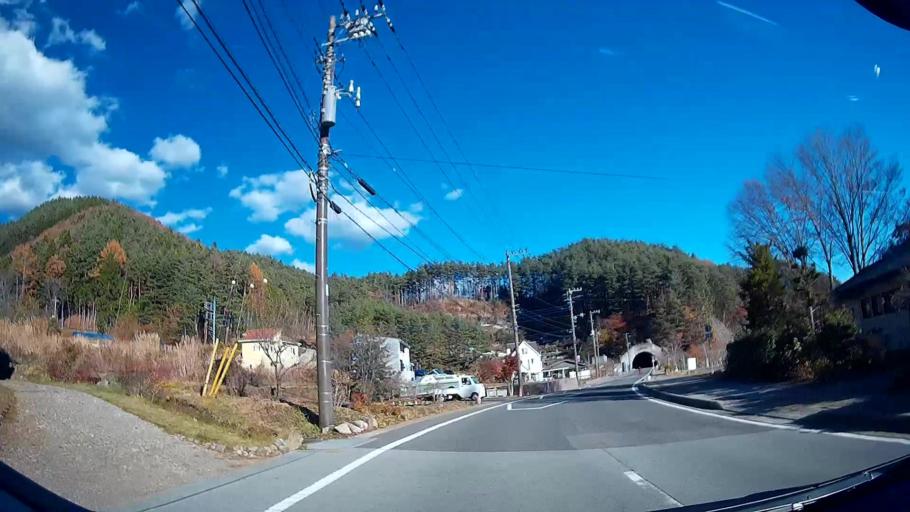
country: JP
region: Yamanashi
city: Fujikawaguchiko
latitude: 35.5113
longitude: 138.7184
